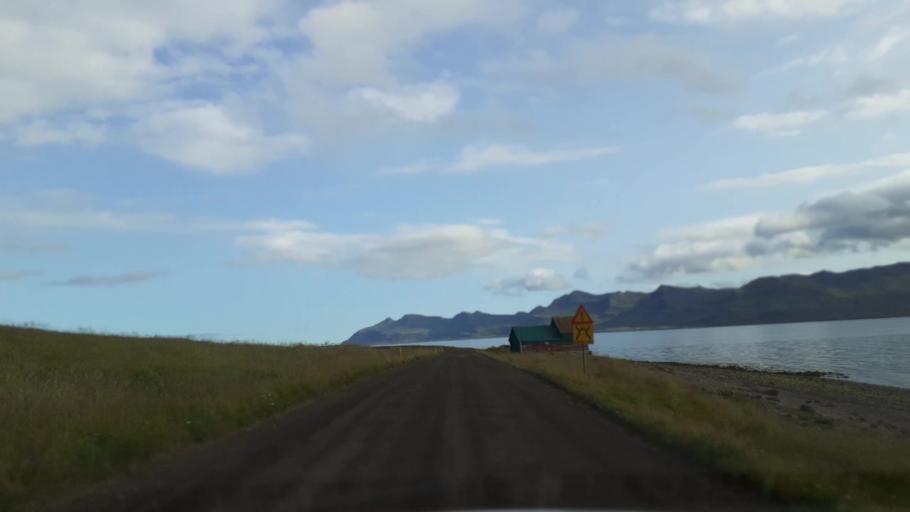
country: IS
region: East
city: Eskifjoerdur
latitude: 65.0370
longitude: -13.8756
